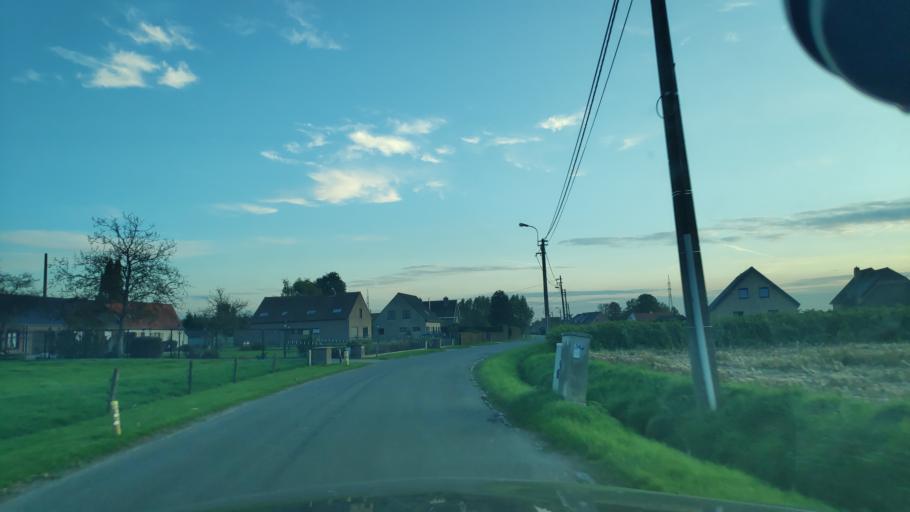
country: BE
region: Flanders
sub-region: Provincie Oost-Vlaanderen
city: Zomergem
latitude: 51.1201
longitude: 3.5045
